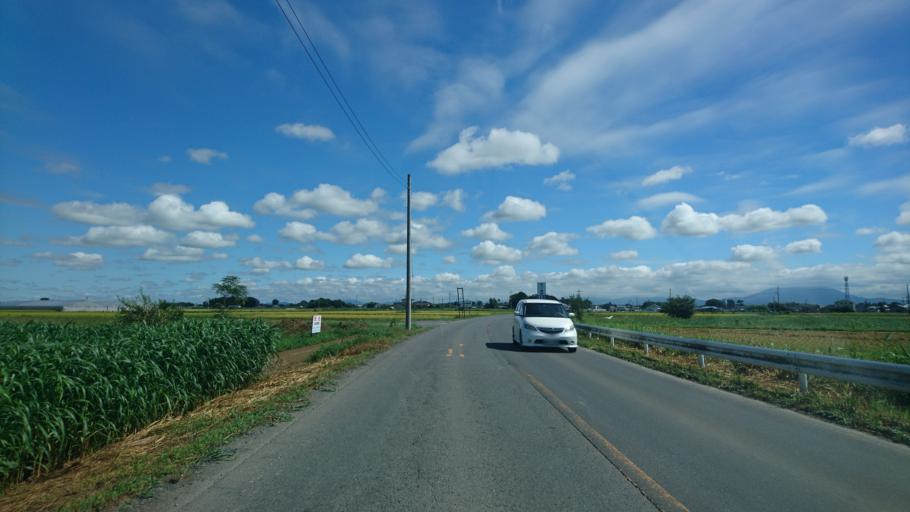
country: JP
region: Ibaraki
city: Yuki
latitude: 36.2160
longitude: 139.9011
